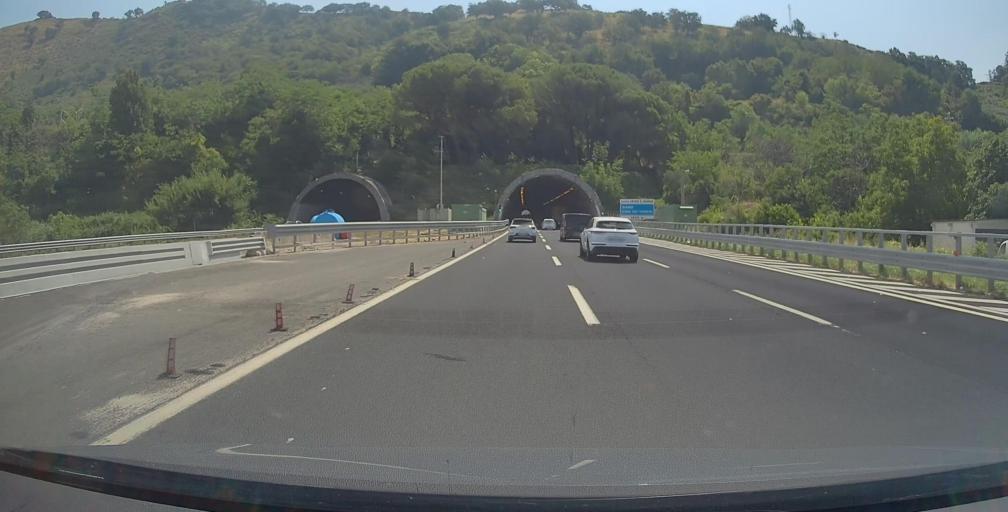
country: IT
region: Campania
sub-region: Provincia di Salerno
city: Nocera Inferiore
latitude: 40.7747
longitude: 14.6500
